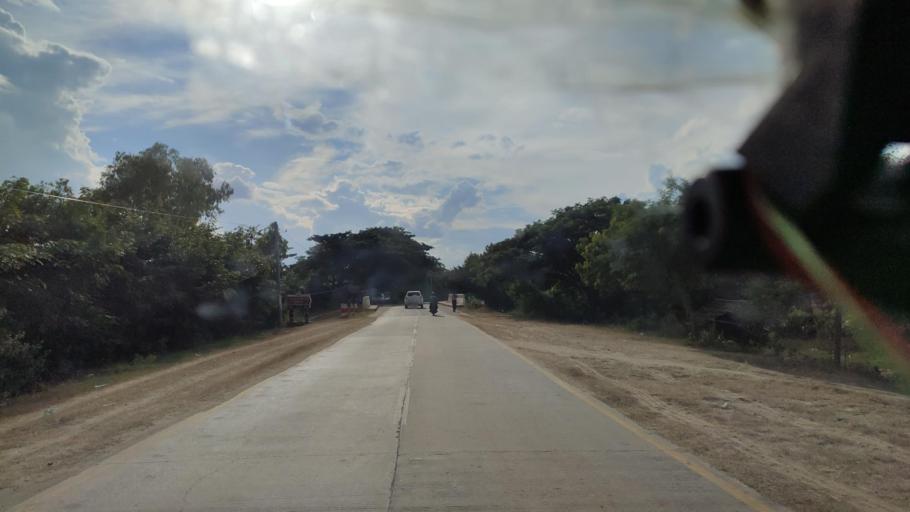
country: MM
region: Mandalay
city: Yamethin
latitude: 20.1604
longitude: 96.1480
